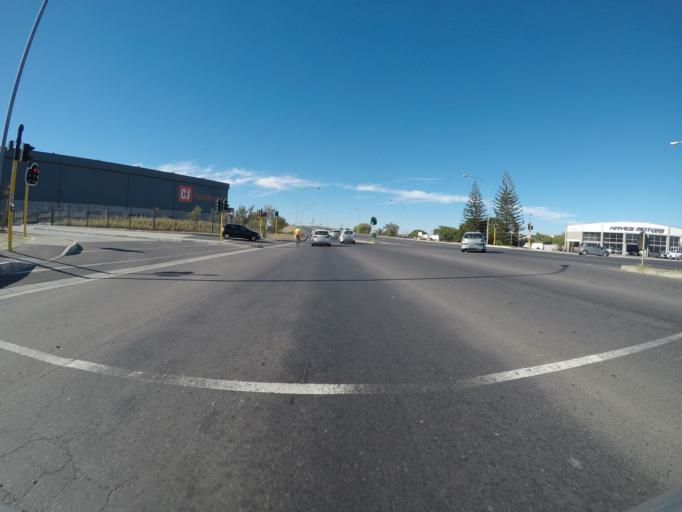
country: ZA
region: Western Cape
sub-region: City of Cape Town
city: Kraaifontein
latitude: -33.8959
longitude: 18.6719
